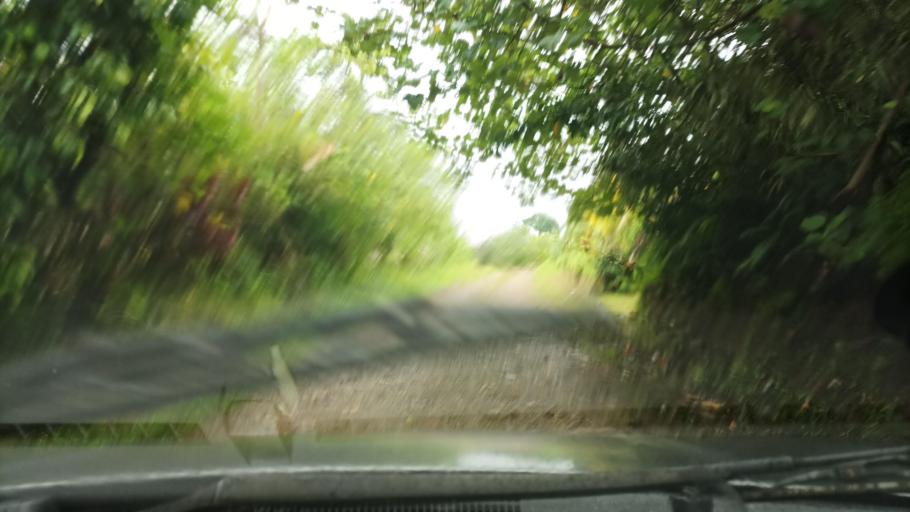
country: FM
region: Pohnpei
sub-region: Sokehs Municipality
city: Palikir - National Government Center
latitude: 6.8517
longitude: 158.1825
